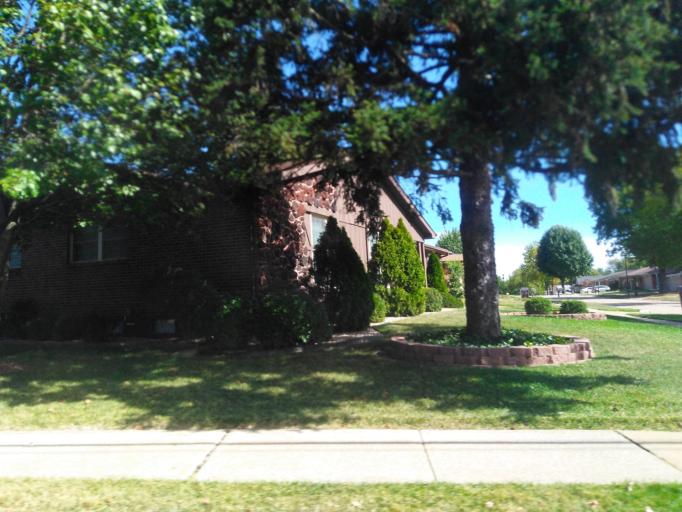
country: US
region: Missouri
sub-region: Saint Louis County
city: Concord
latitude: 38.4878
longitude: -90.3674
